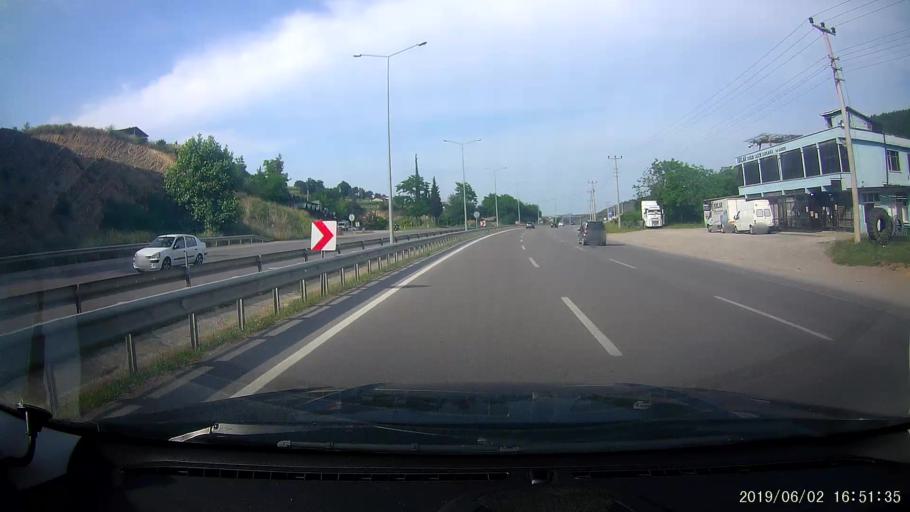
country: TR
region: Samsun
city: Taflan
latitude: 41.2758
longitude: 36.1841
